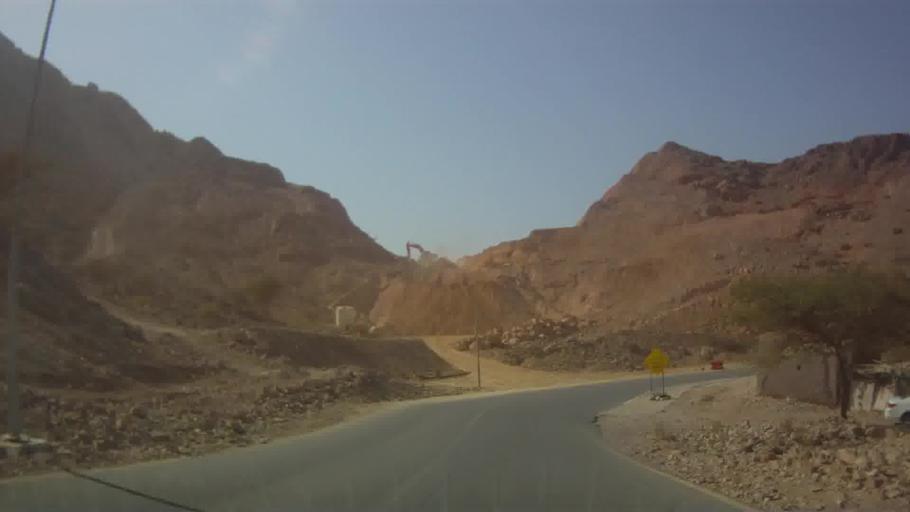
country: OM
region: Muhafazat Masqat
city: Muscat
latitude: 23.5072
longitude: 58.7281
